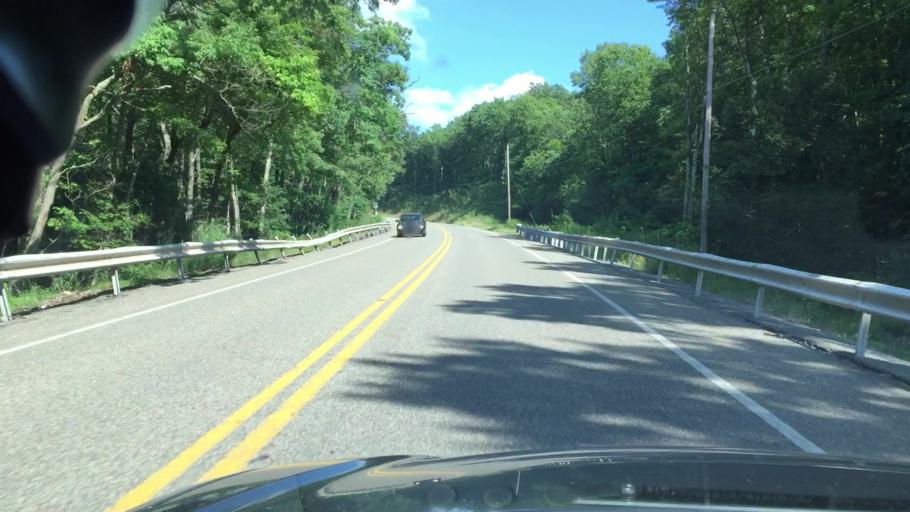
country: US
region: Pennsylvania
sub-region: Carbon County
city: Weatherly
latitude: 40.9124
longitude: -75.8463
